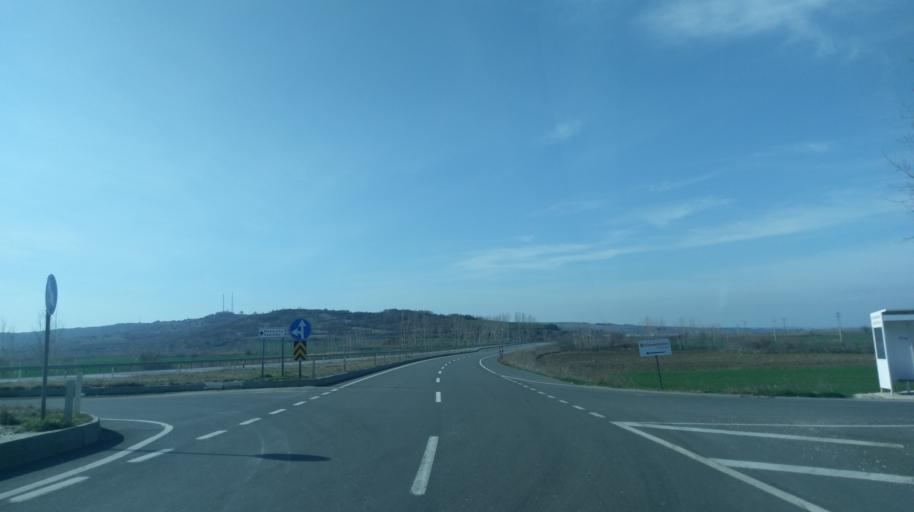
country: TR
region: Edirne
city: Hamidiye
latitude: 41.1137
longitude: 26.6492
